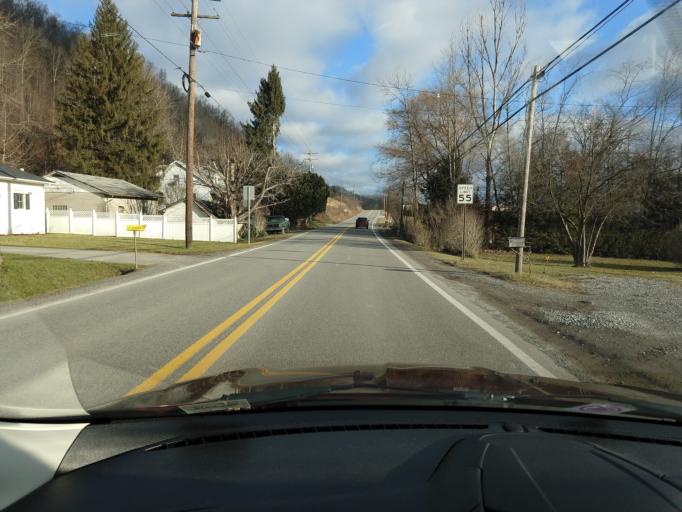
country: US
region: West Virginia
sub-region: Randolph County
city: Elkins
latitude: 38.7380
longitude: -79.9667
